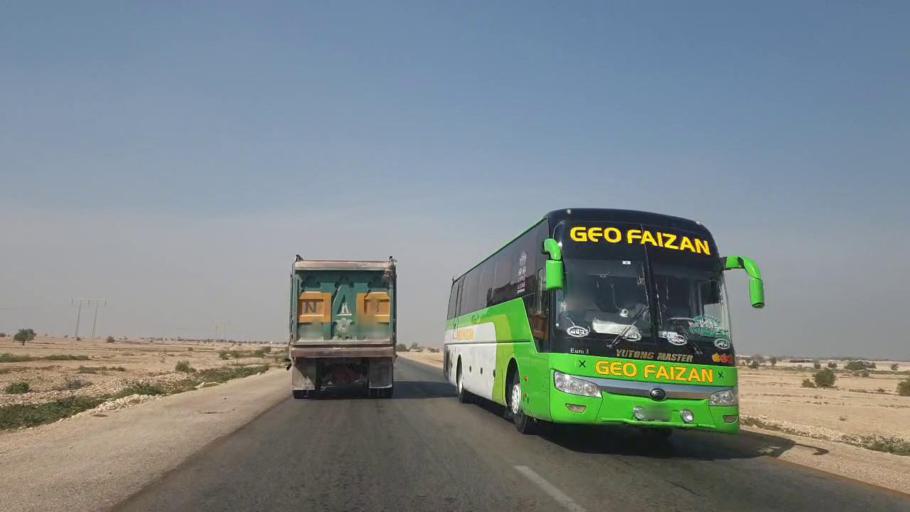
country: PK
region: Sindh
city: Hala
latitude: 25.8330
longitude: 68.2695
